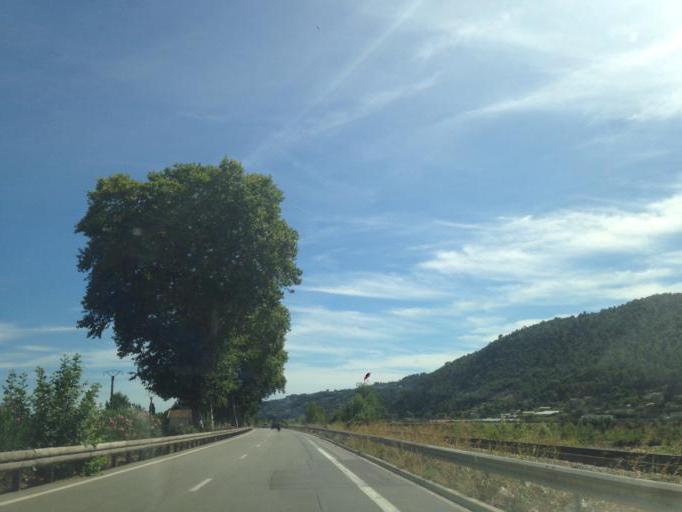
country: FR
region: Provence-Alpes-Cote d'Azur
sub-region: Departement des Alpes-Maritimes
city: Gattieres
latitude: 43.7416
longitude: 7.1847
